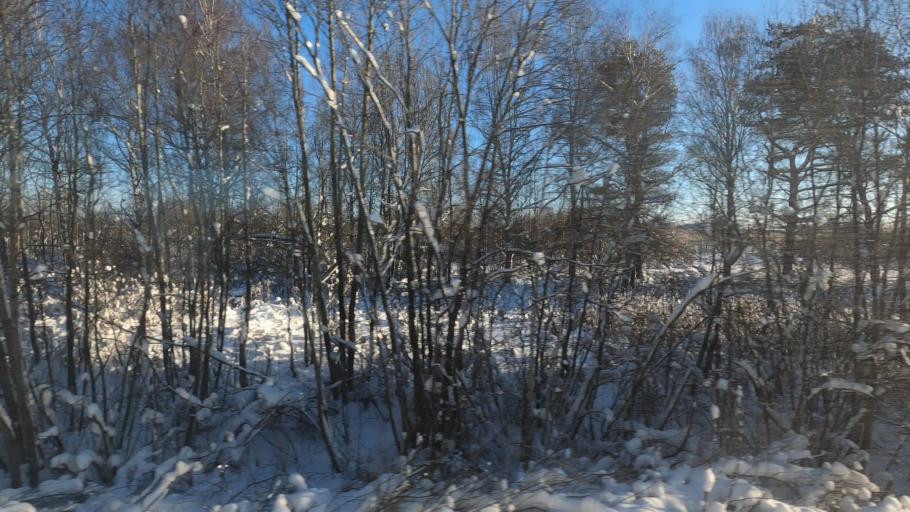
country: RU
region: Moskovskaya
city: Orud'yevo
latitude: 56.4282
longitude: 37.4989
